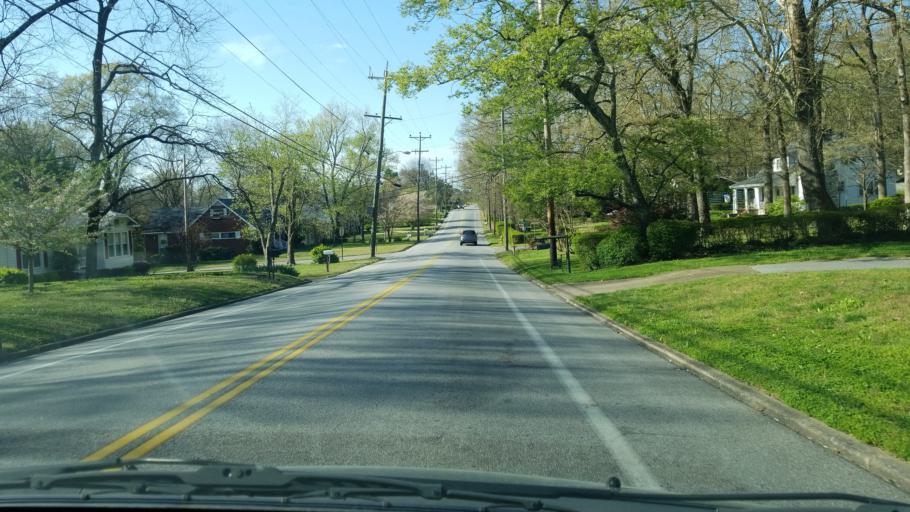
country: US
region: Tennessee
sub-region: Hamilton County
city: East Ridge
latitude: 35.0164
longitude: -85.2411
